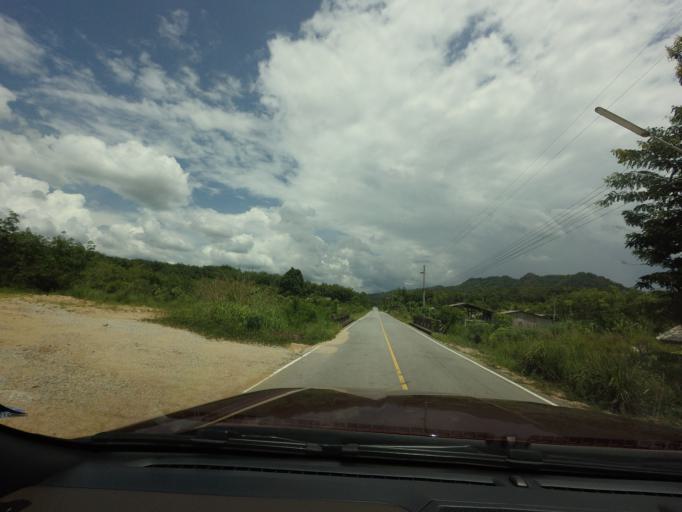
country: TH
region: Narathiwat
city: Chanae
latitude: 6.0664
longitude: 101.6877
